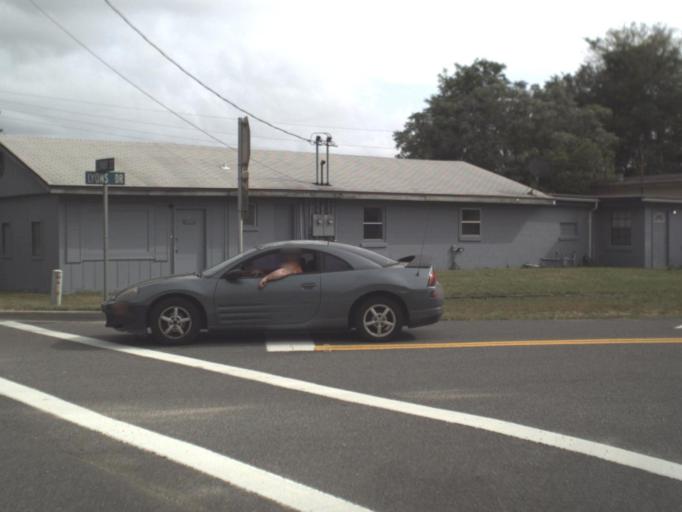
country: US
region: Florida
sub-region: Santa Rosa County
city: Milton
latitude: 30.6585
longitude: -87.0485
